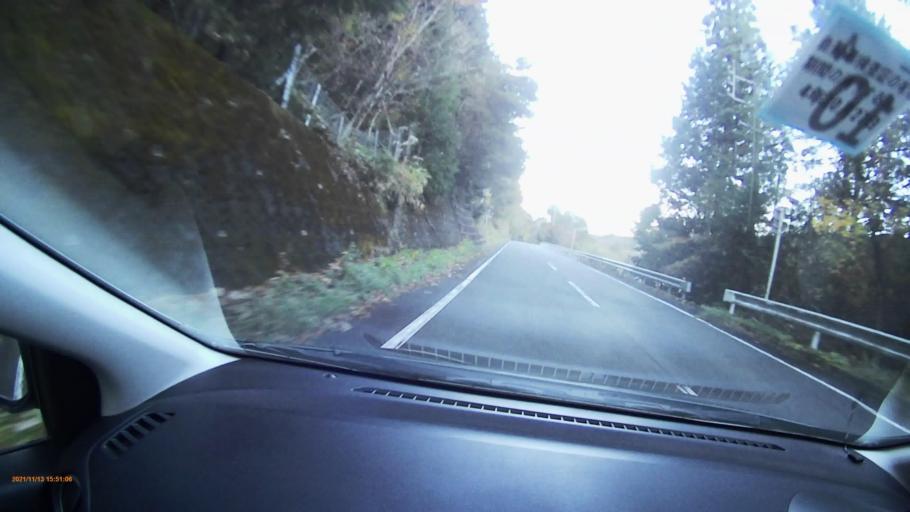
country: JP
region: Gifu
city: Nakatsugawa
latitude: 35.5969
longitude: 137.4178
